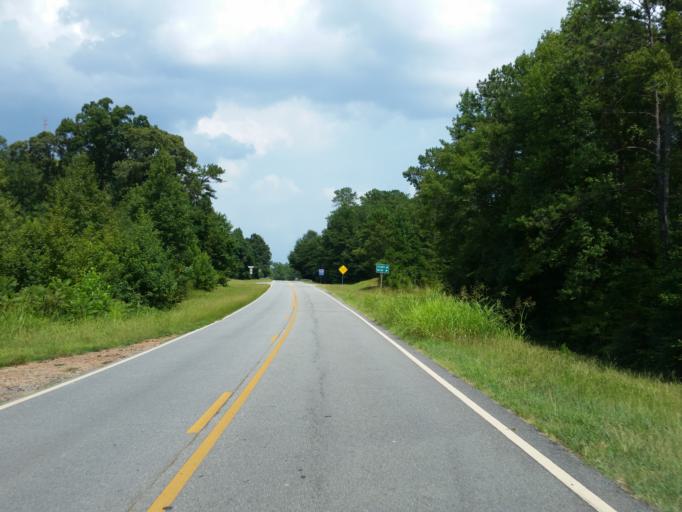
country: US
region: Georgia
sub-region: Monroe County
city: Forsyth
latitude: 33.1121
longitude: -84.0058
